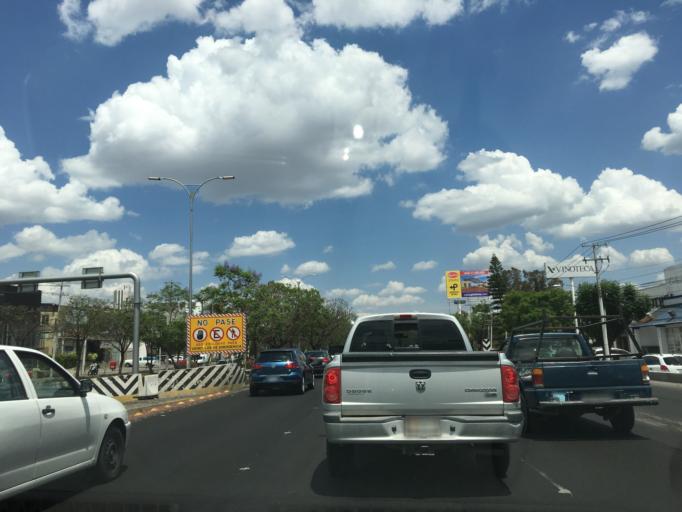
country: MX
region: Queretaro
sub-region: Queretaro
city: Santiago de Queretaro
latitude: 20.6122
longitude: -100.3836
